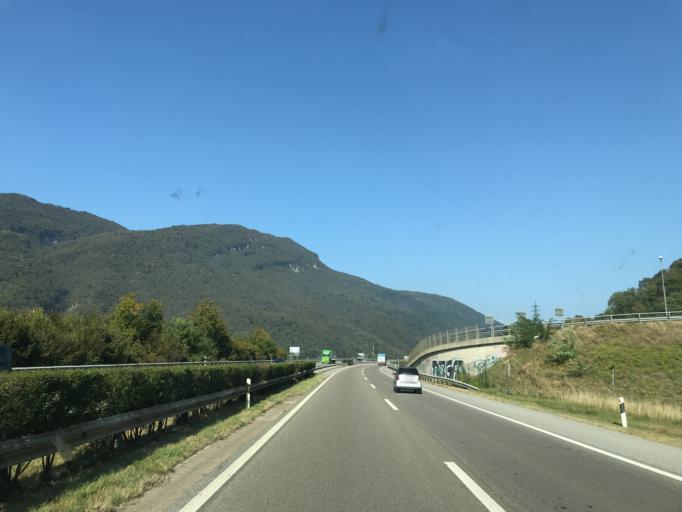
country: CH
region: Ticino
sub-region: Mendrisio District
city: Riva San Vitale
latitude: 45.8871
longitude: 8.9787
